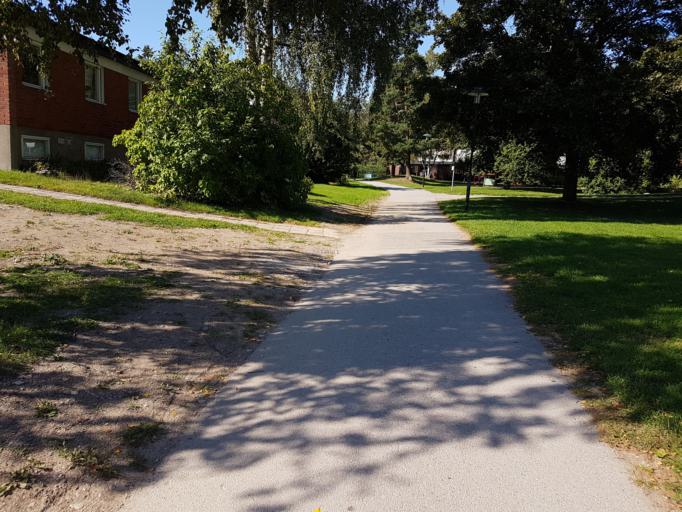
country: SE
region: Stockholm
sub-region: Huddinge Kommun
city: Huddinge
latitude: 59.2632
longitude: 18.0024
